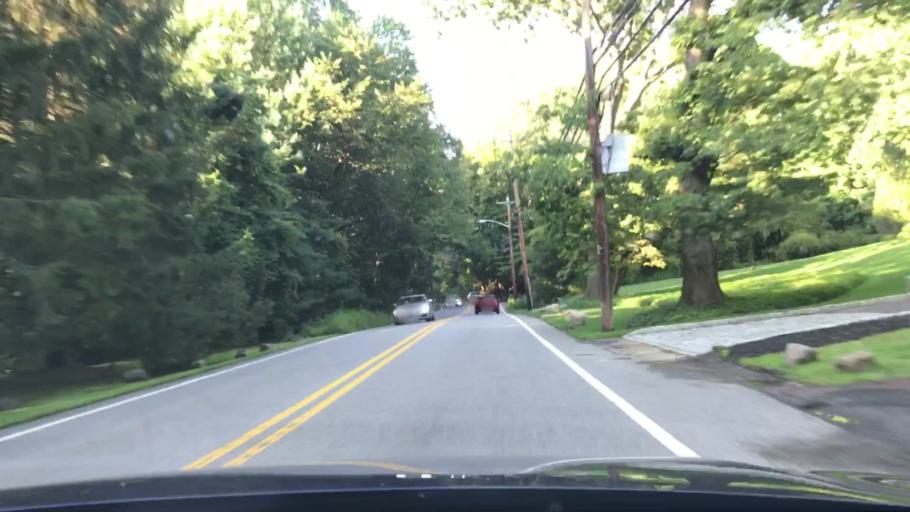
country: US
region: New Jersey
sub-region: Bergen County
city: Northvale
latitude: 40.9888
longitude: -73.9355
